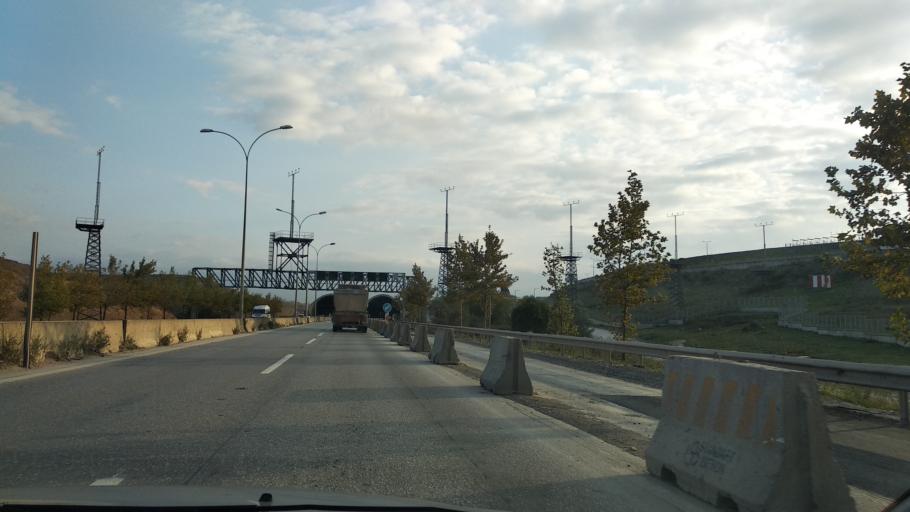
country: TR
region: Istanbul
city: Pendik
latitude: 40.9064
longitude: 29.3275
